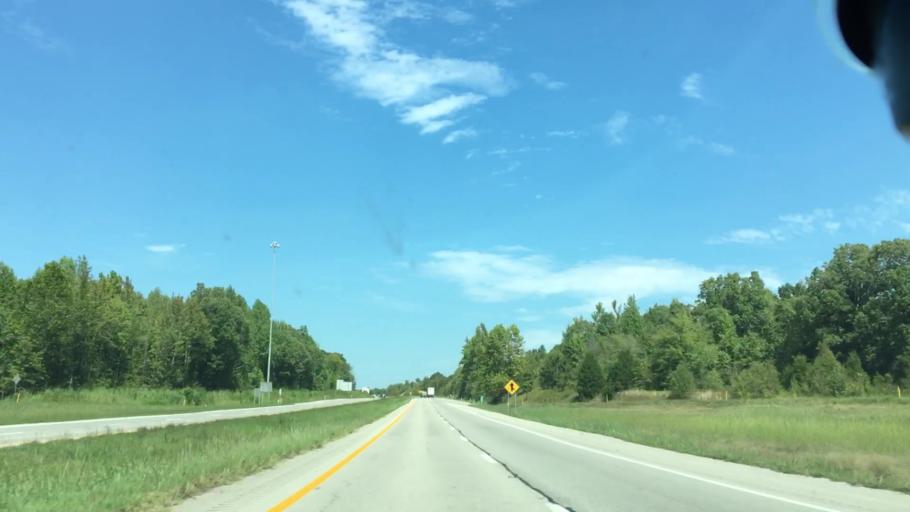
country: US
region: Kentucky
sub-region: Hopkins County
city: Nortonville
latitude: 37.1929
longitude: -87.4415
